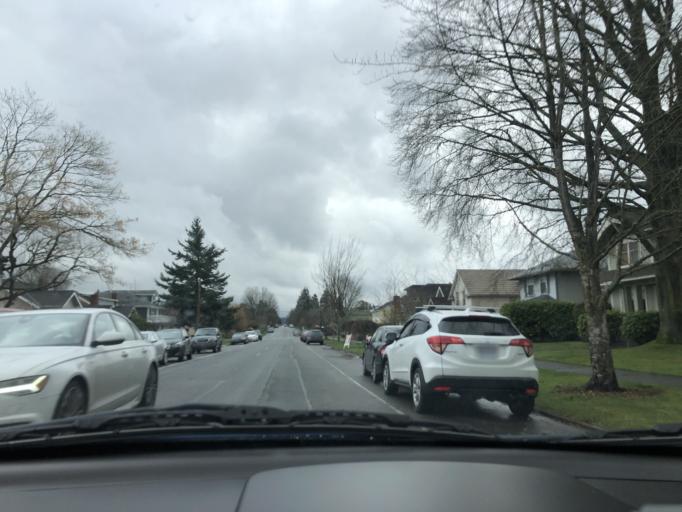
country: US
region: Washington
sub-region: Snohomish County
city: Everett
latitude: 47.9991
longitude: -122.2110
